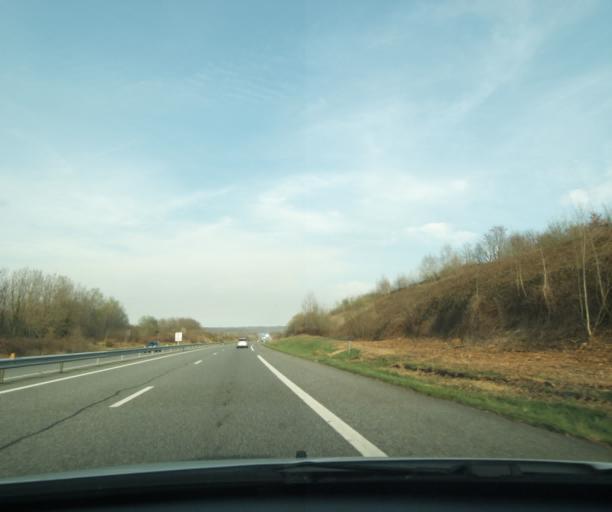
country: FR
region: Midi-Pyrenees
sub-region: Departement de la Haute-Garonne
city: Montrejeau
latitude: 43.1014
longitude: 0.5853
